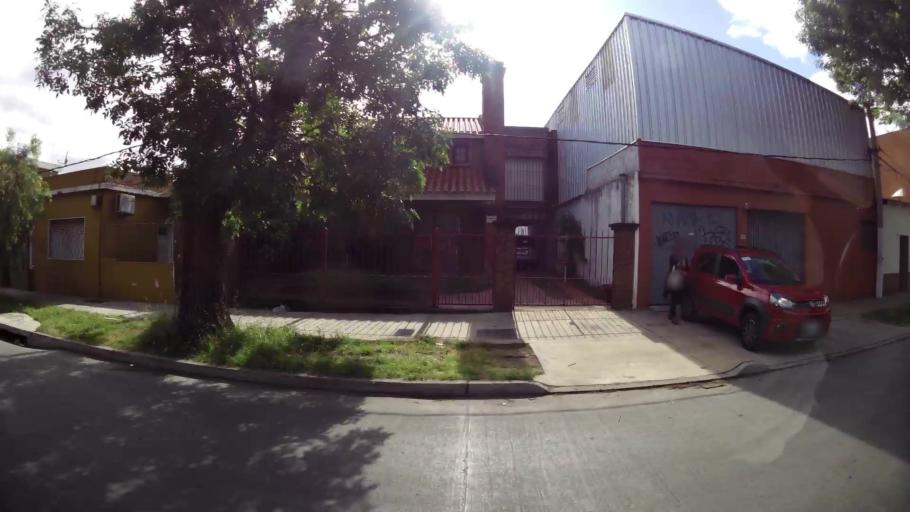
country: UY
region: Montevideo
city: Montevideo
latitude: -34.8817
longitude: -56.1650
